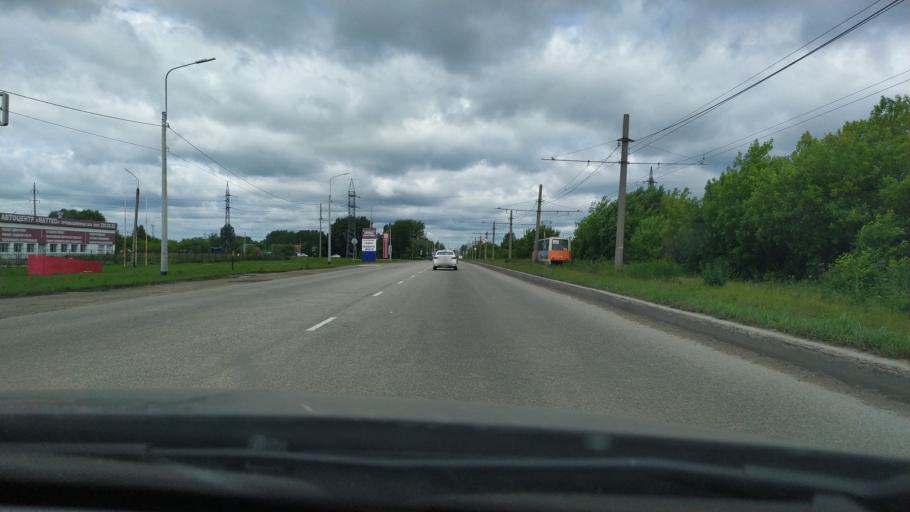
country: RU
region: Perm
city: Kondratovo
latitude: 57.9301
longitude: 56.1292
